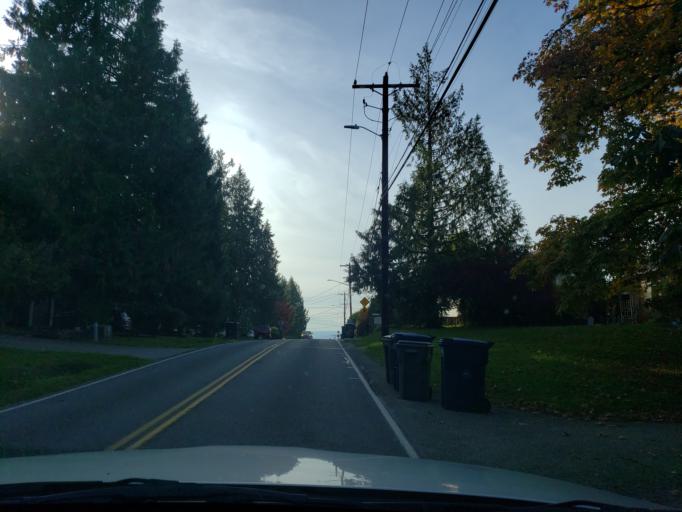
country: US
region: Washington
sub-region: Snohomish County
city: Mukilteo
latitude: 47.9294
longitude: -122.2938
